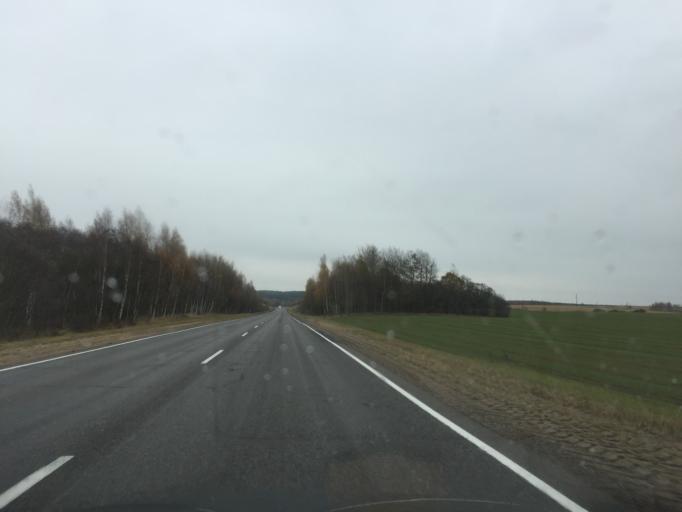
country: BY
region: Mogilev
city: Cherykaw
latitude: 53.5931
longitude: 31.3847
